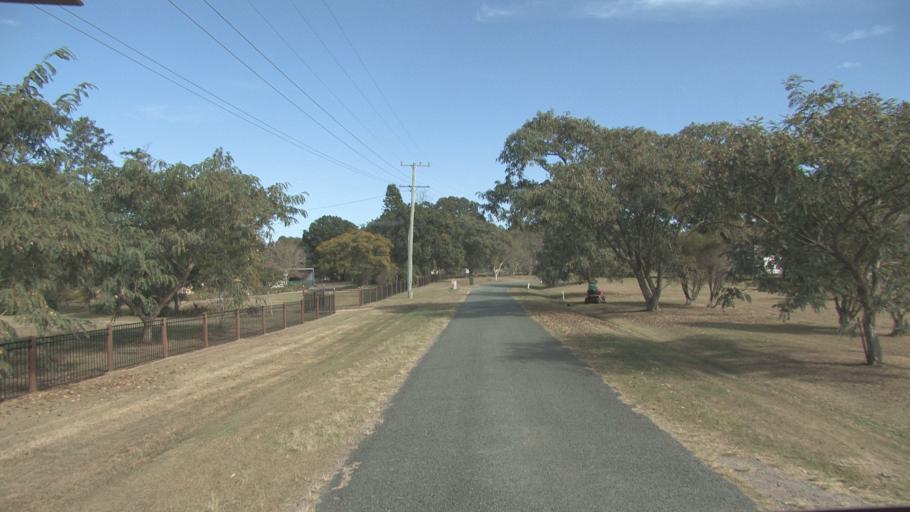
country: AU
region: Queensland
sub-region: Logan
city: North Maclean
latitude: -27.7759
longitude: 152.9958
